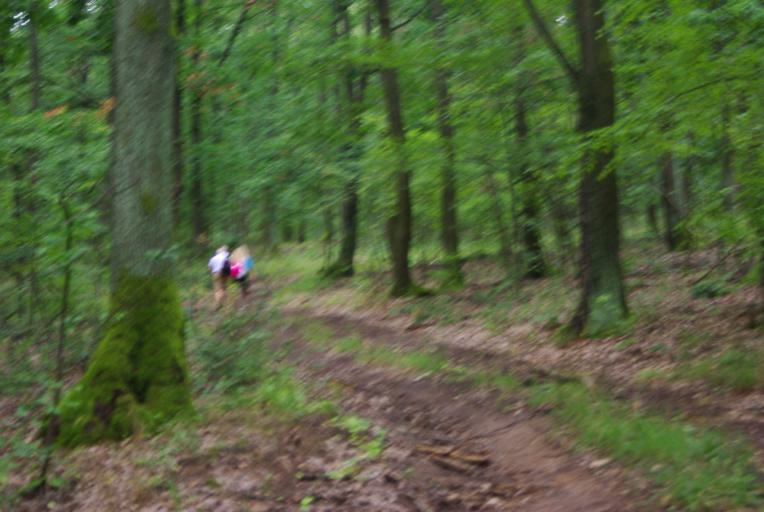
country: HU
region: Nograd
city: Bujak
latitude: 47.9322
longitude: 19.6046
